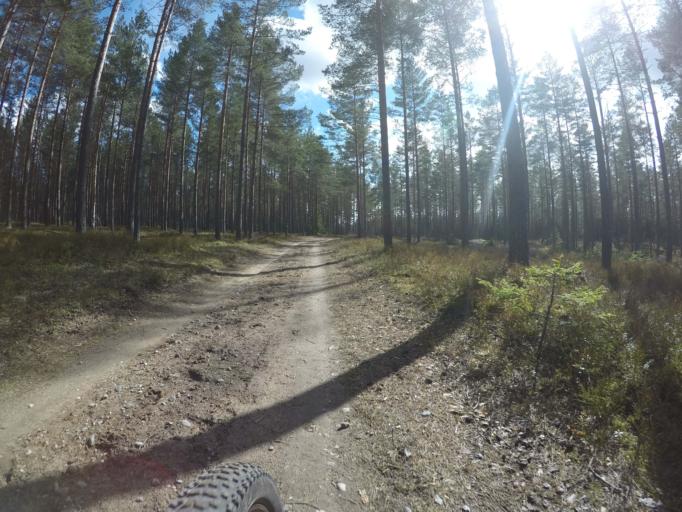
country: SE
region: Vaestmanland
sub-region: Kungsors Kommun
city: Kungsoer
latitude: 59.3611
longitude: 16.1089
